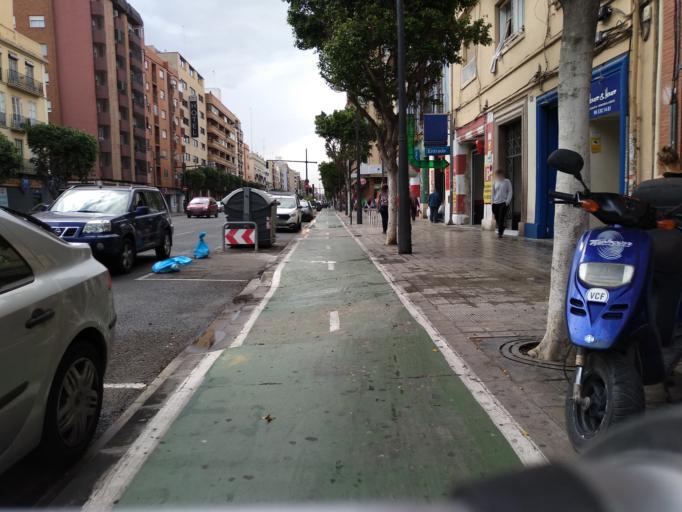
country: ES
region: Valencia
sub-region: Provincia de Valencia
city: Valencia
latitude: 39.4629
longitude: -0.3420
